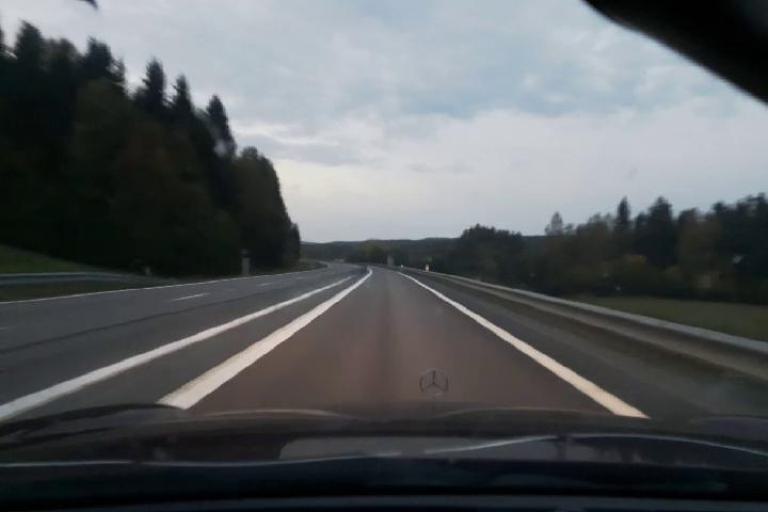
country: SE
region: Vaesternorrland
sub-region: Kramfors Kommun
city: Nordingra
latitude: 62.9722
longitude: 18.1608
